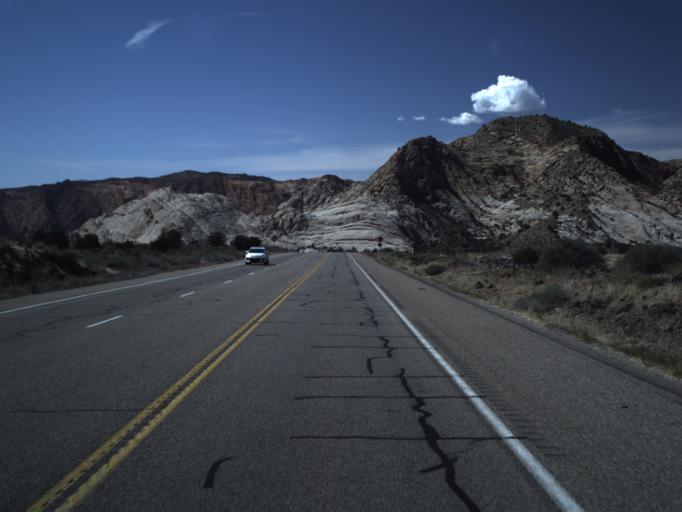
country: US
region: Utah
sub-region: Washington County
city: Ivins
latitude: 37.2445
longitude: -113.6322
